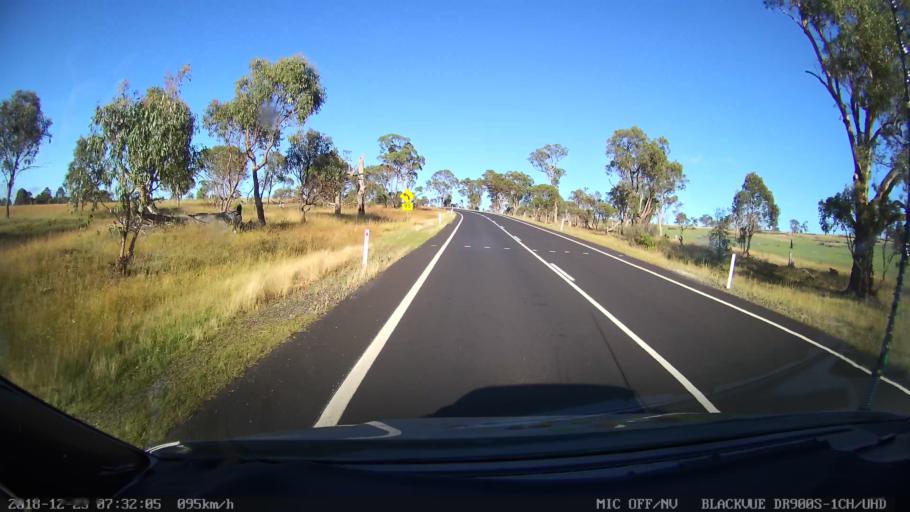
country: AU
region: New South Wales
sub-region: Armidale Dumaresq
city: Enmore
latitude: -30.5034
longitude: 152.1225
